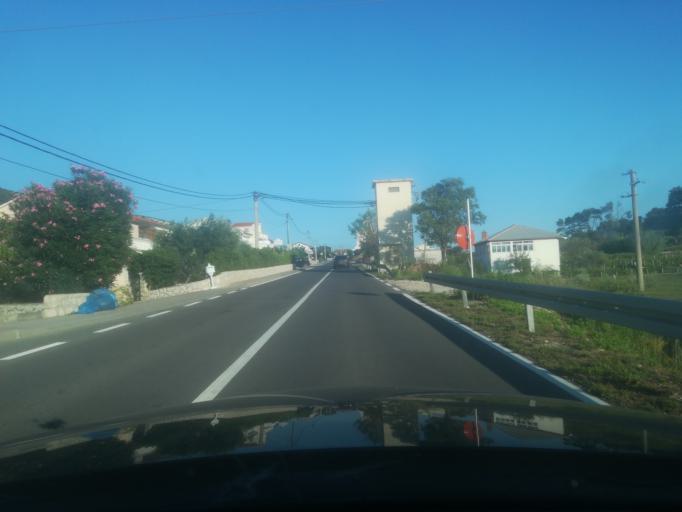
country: HR
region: Primorsko-Goranska
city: Banjol
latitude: 44.7718
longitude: 14.7617
